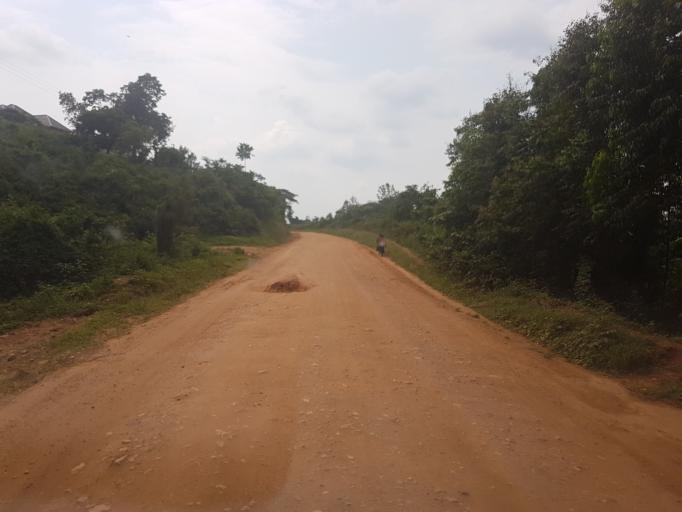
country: UG
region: Western Region
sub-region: Kanungu District
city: Ntungamo
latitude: -0.8231
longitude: 29.7093
